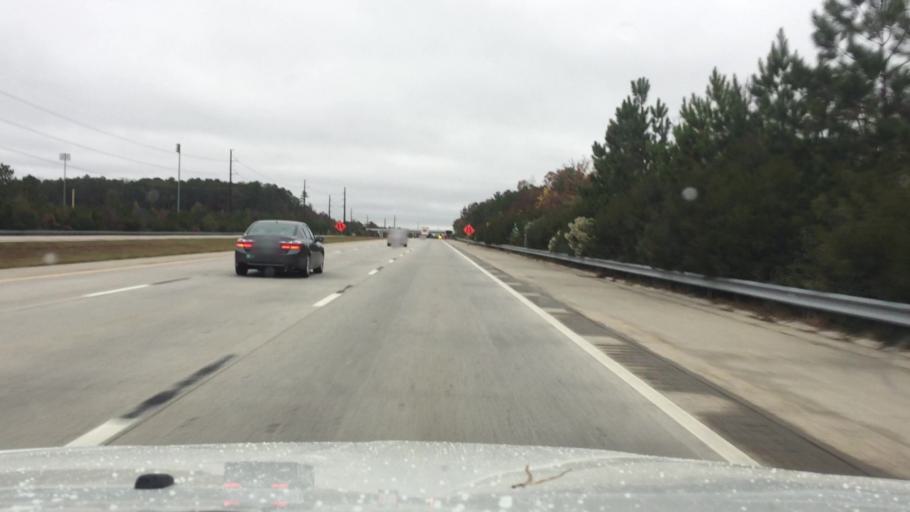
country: US
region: North Carolina
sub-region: Wake County
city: Green Level
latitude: 35.7955
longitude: -78.8892
